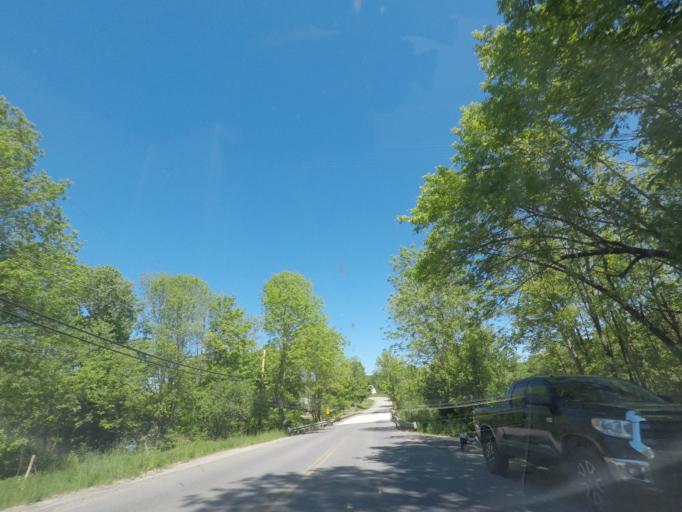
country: US
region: Maine
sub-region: Kennebec County
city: Manchester
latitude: 44.2443
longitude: -69.8945
